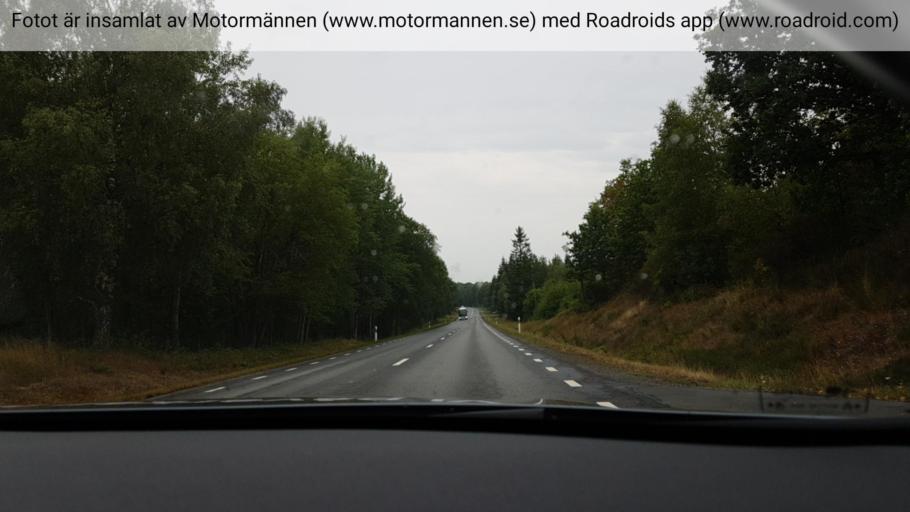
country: SE
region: Joenkoeping
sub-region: Varnamo Kommun
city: Varnamo
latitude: 57.2268
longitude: 14.1382
